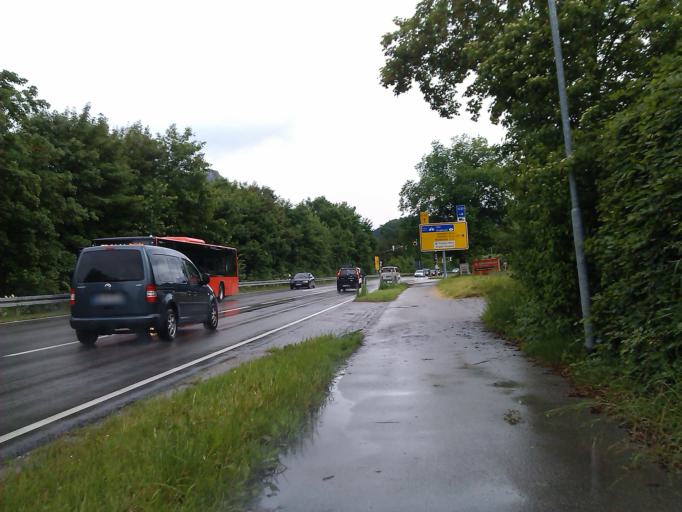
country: DE
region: Bavaria
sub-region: Swabia
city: Fuessen
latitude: 47.5843
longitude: 10.7072
